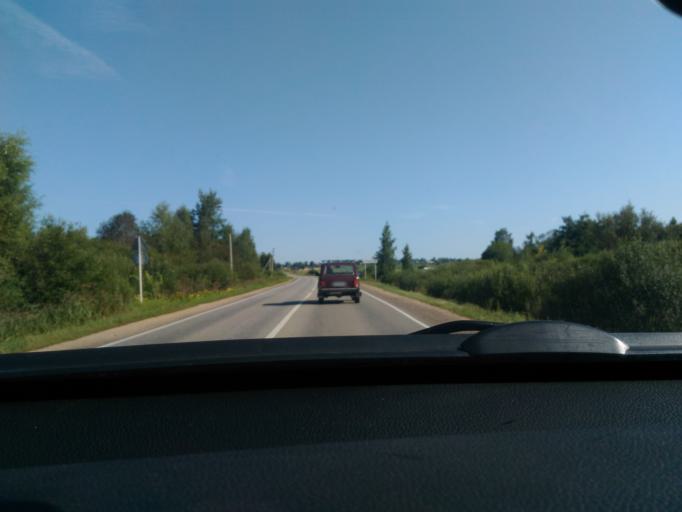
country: RU
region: Moskovskaya
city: Podosinki
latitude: 56.2285
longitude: 37.5491
